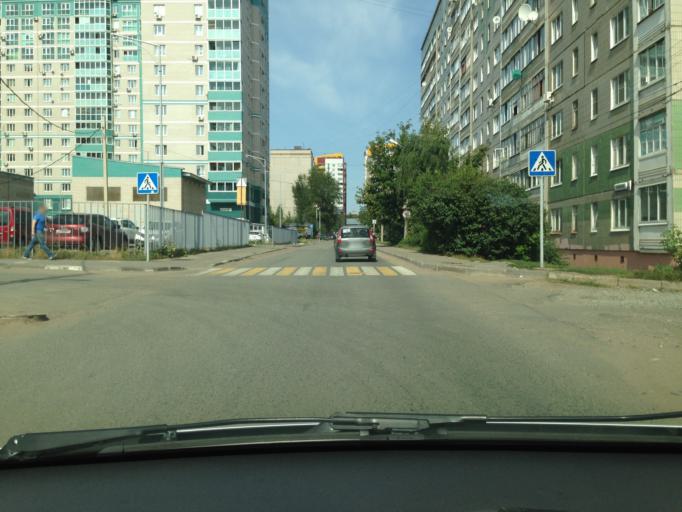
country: RU
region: Udmurtiya
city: Izhevsk
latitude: 56.8686
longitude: 53.1875
